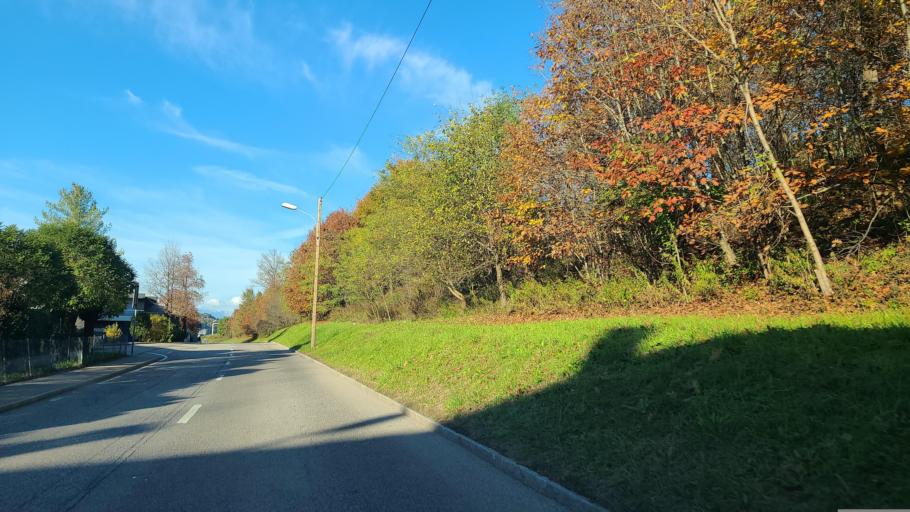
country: CH
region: Ticino
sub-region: Lugano District
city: Montagnola
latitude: 45.9630
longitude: 8.9254
